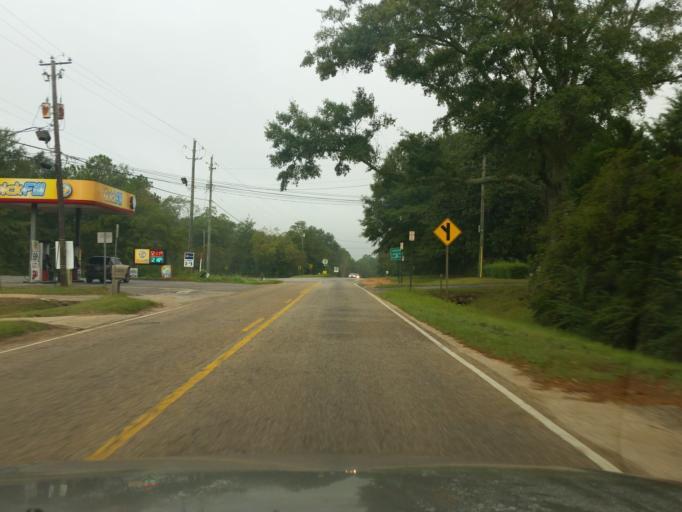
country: US
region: Florida
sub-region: Escambia County
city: Cantonment
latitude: 30.6077
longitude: -87.3620
